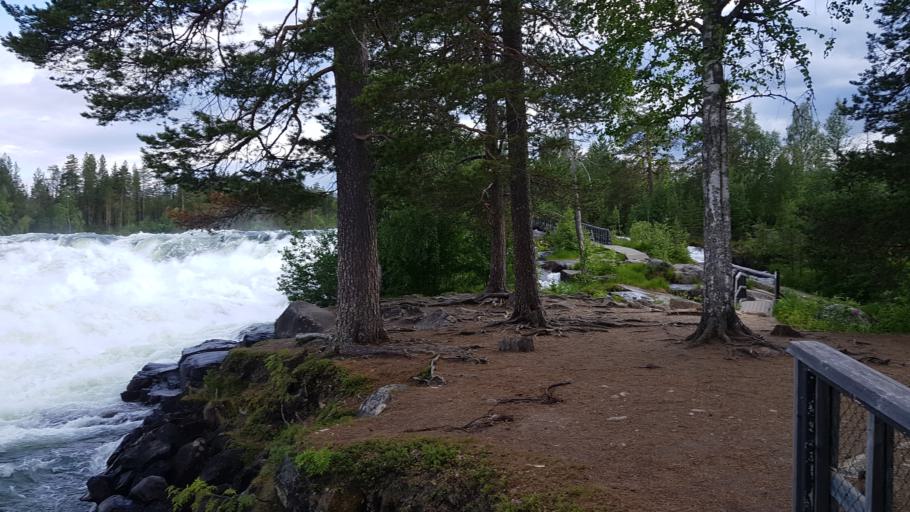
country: SE
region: Norrbotten
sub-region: Alvsbyns Kommun
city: AElvsbyn
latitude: 65.8512
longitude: 20.4082
